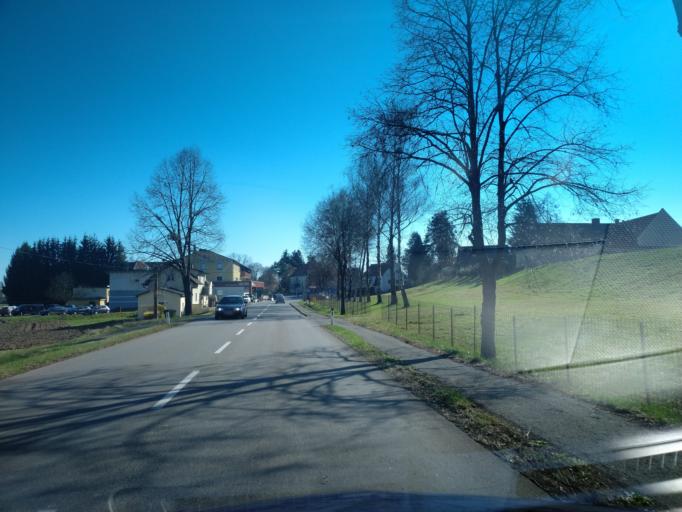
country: AT
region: Styria
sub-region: Politischer Bezirk Leibnitz
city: Stocking
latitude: 46.8646
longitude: 15.5285
